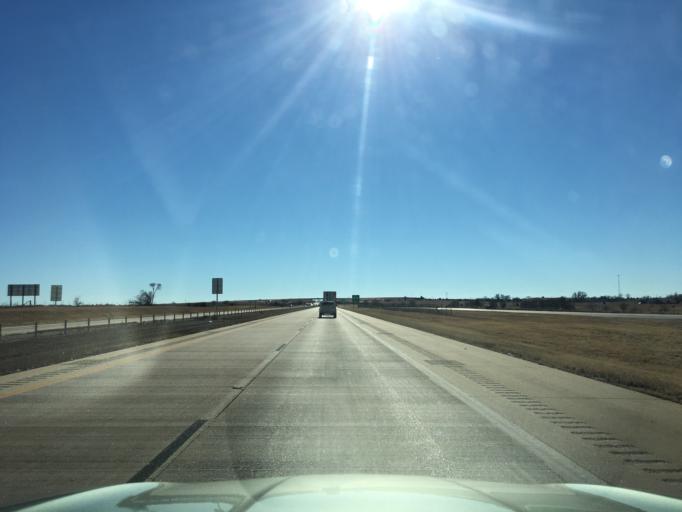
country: US
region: Oklahoma
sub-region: Noble County
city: Perry
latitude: 36.4144
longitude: -97.3272
